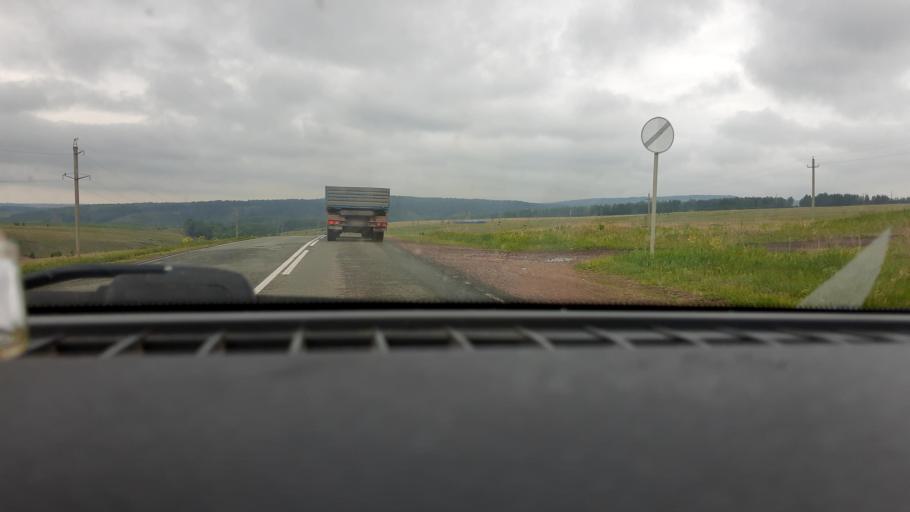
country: RU
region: Bashkortostan
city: Priyutovo
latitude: 53.9805
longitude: 53.9875
